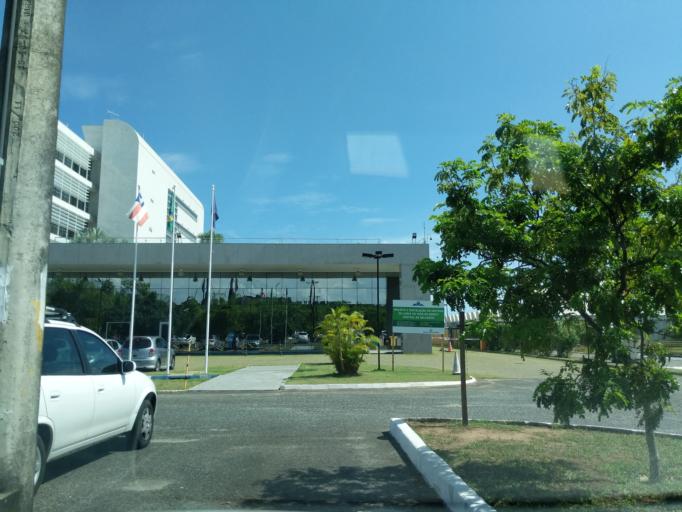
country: BR
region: Bahia
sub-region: Salvador
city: Salvador
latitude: -12.9501
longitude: -38.4272
